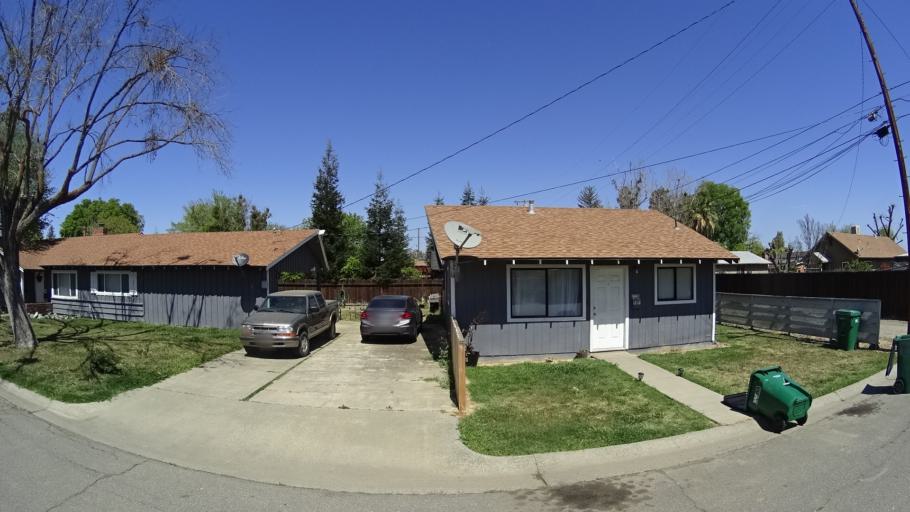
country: US
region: California
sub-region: Glenn County
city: Willows
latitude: 39.5255
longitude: -122.2038
